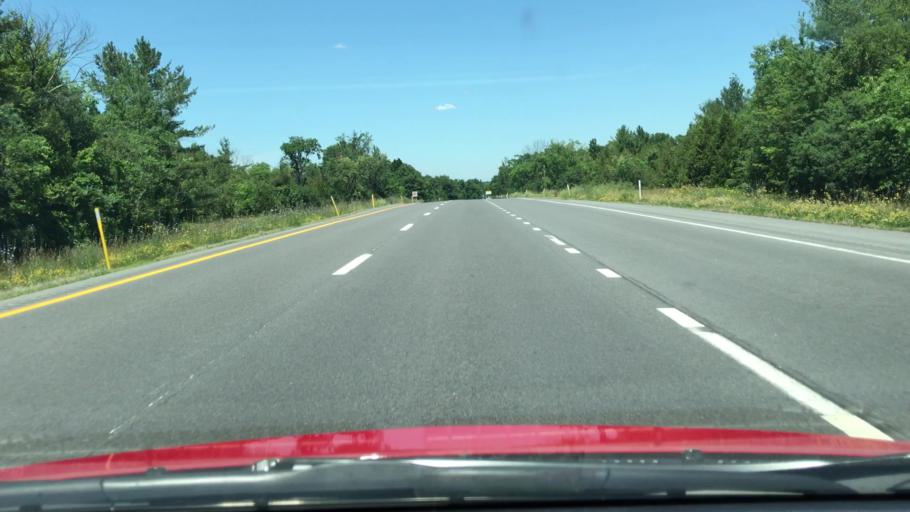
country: US
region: New York
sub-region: Clinton County
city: Cumberland Head
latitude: 44.8090
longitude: -73.4450
